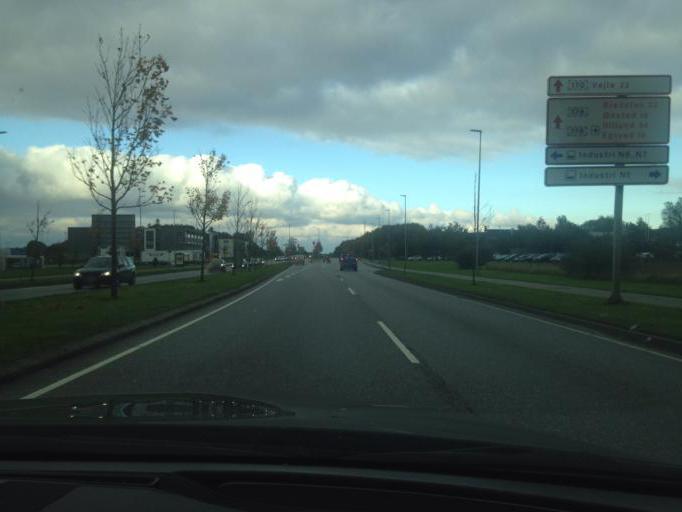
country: DK
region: South Denmark
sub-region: Kolding Kommune
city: Kolding
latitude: 55.5309
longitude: 9.4678
